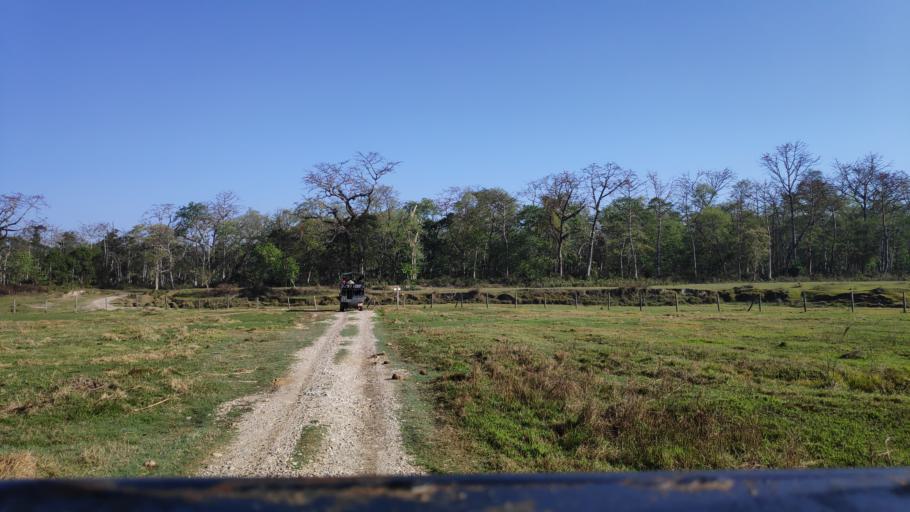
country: NP
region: Central Region
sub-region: Narayani Zone
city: Bharatpur
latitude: 27.5615
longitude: 84.5222
